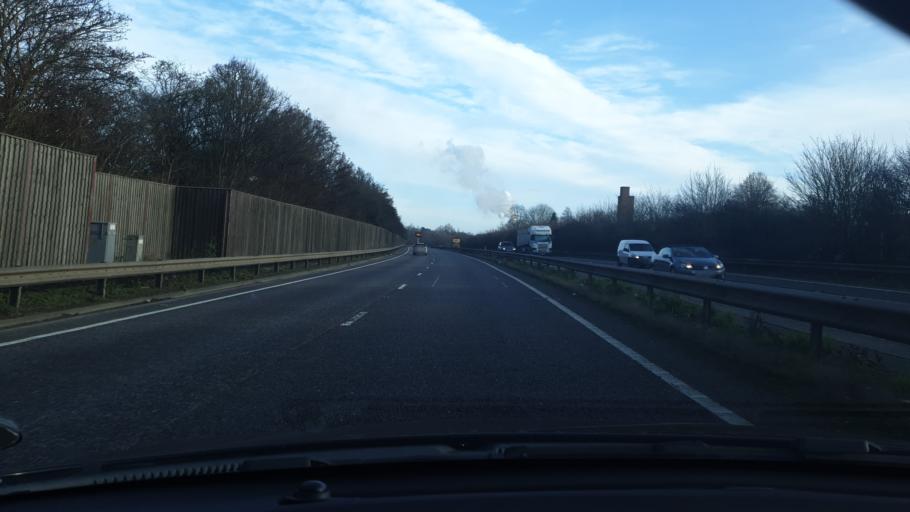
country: GB
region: England
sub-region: Suffolk
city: Bury St Edmunds
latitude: 52.2531
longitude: 0.6939
